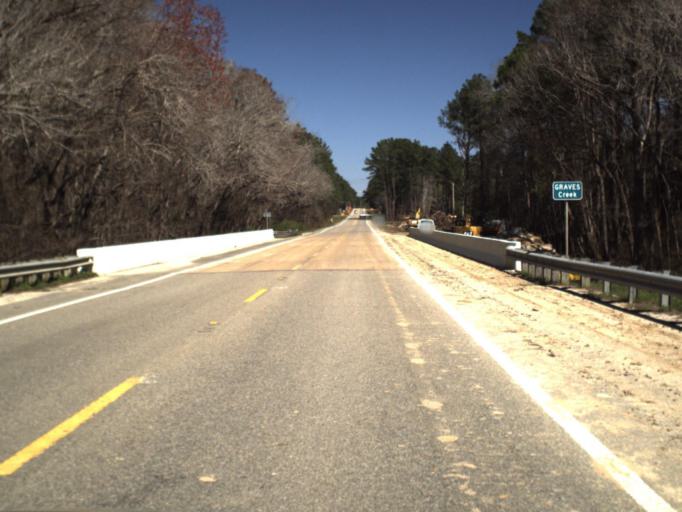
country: US
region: Florida
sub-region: Calhoun County
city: Blountstown
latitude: 30.5285
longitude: -85.0300
